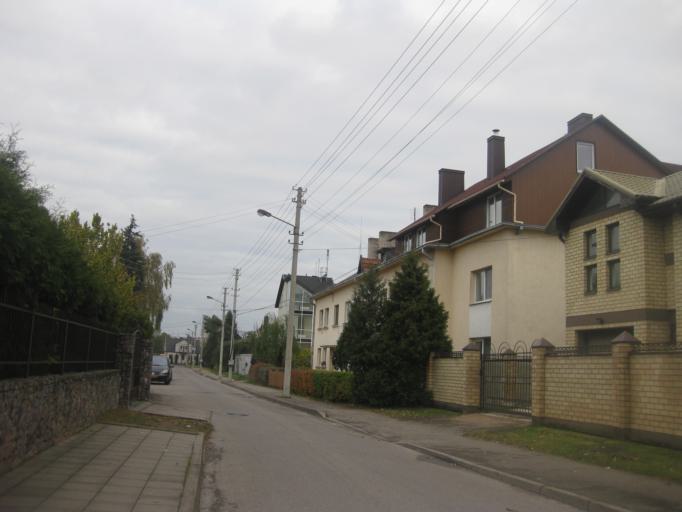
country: LT
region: Kauno apskritis
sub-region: Kaunas
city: Kaunas
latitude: 54.9105
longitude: 23.9165
